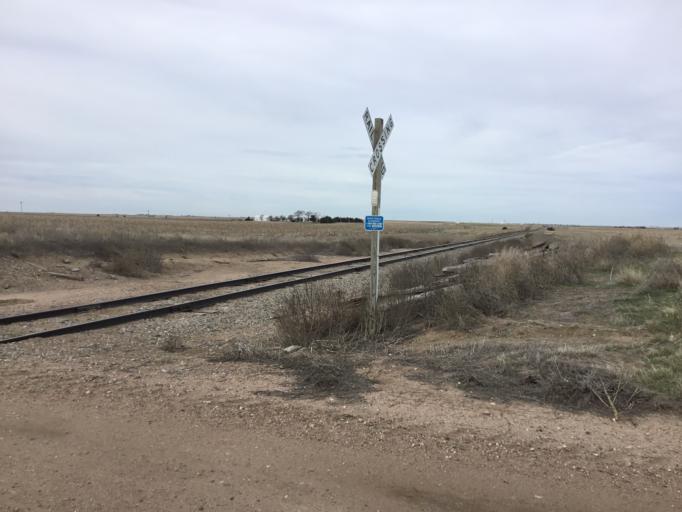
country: US
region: Kansas
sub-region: Sherman County
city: Goodland
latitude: 39.3385
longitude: -101.9488
